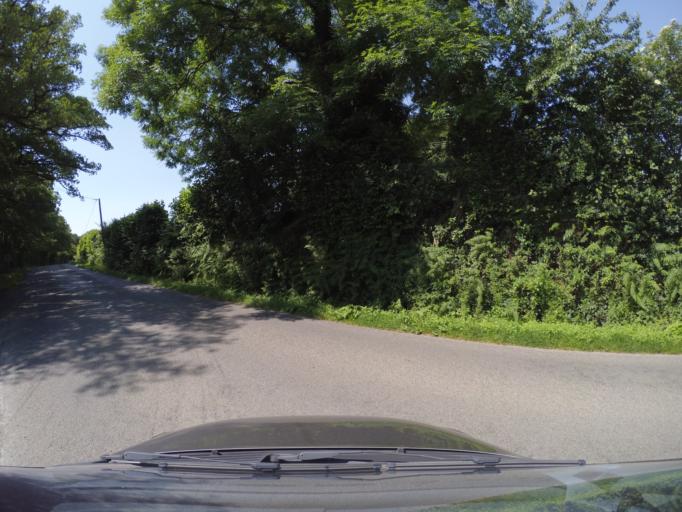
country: FR
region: Pays de la Loire
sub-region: Departement de la Vendee
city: La Flocelliere
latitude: 46.8155
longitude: -0.8533
